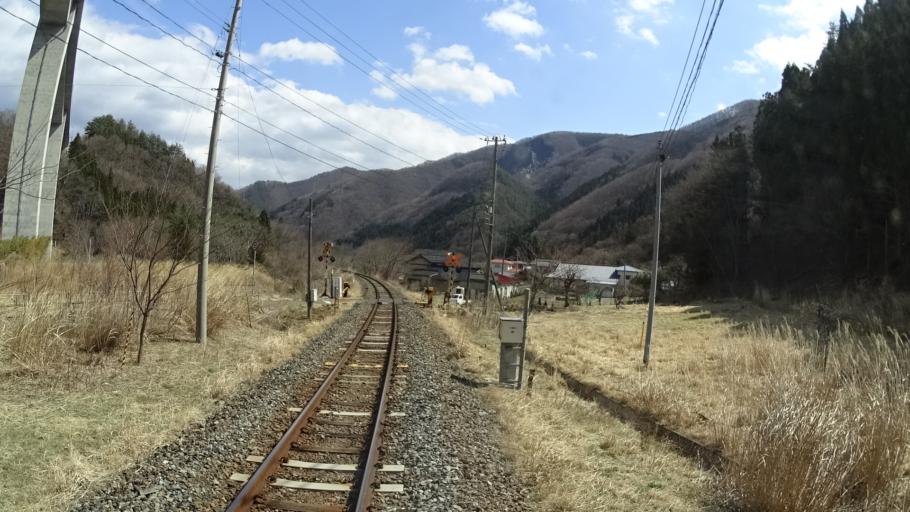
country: JP
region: Iwate
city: Kamaishi
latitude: 39.2515
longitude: 141.7544
